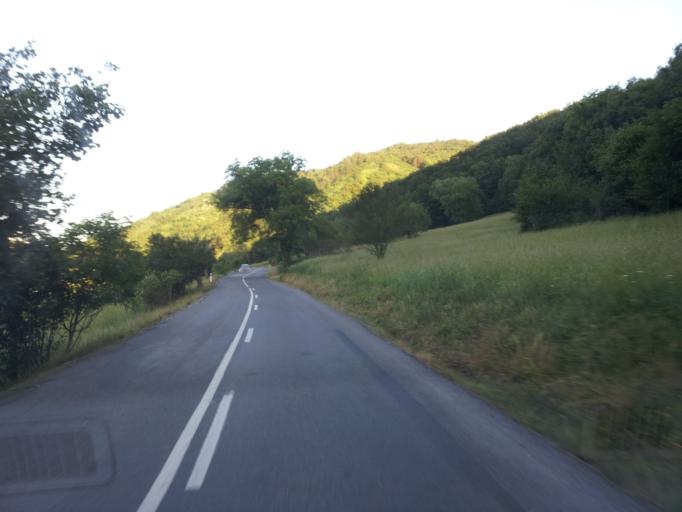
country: SK
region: Banskobystricky
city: Svaety Anton
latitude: 48.3455
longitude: 18.9328
